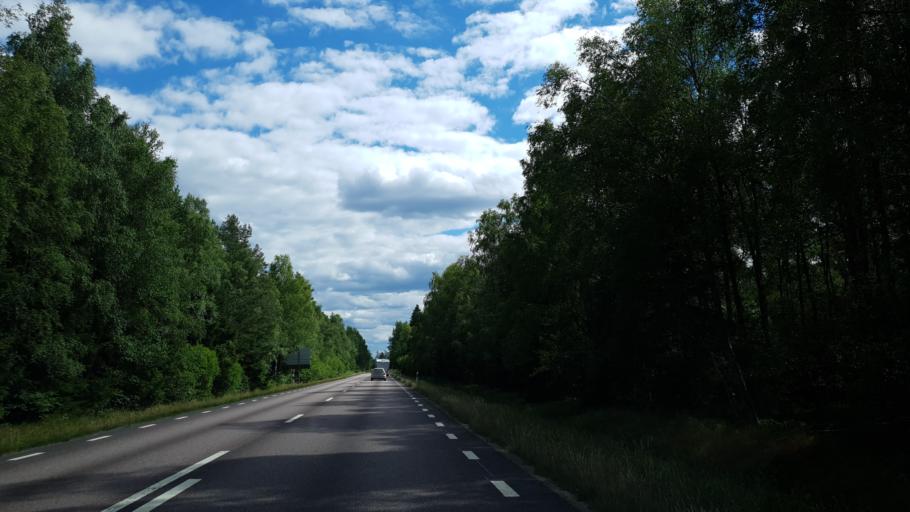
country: SE
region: Kronoberg
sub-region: Lessebo Kommun
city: Lessebo
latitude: 56.8424
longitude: 15.3902
